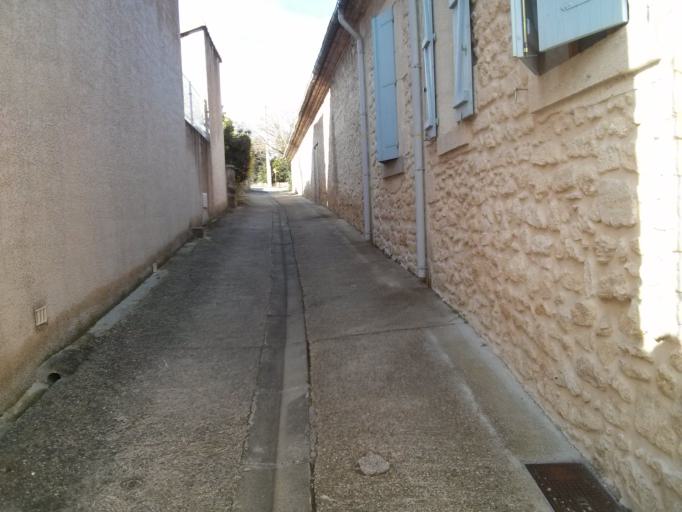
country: FR
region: Languedoc-Roussillon
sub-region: Departement du Gard
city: Aubais
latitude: 43.7714
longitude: 4.1222
